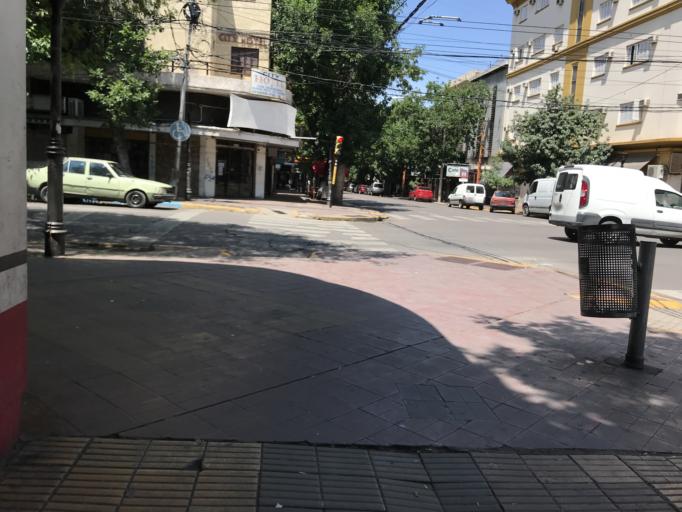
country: AR
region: Mendoza
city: Mendoza
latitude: -32.8850
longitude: -68.8394
